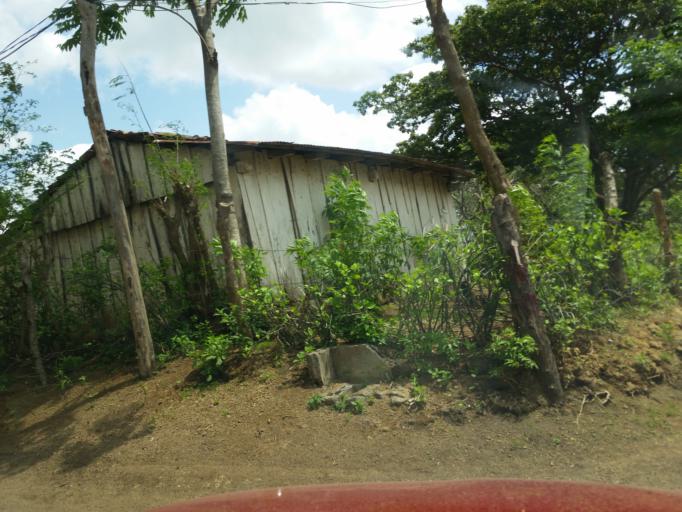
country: NI
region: Masaya
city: Ticuantepe
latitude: 12.0643
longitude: -86.2440
